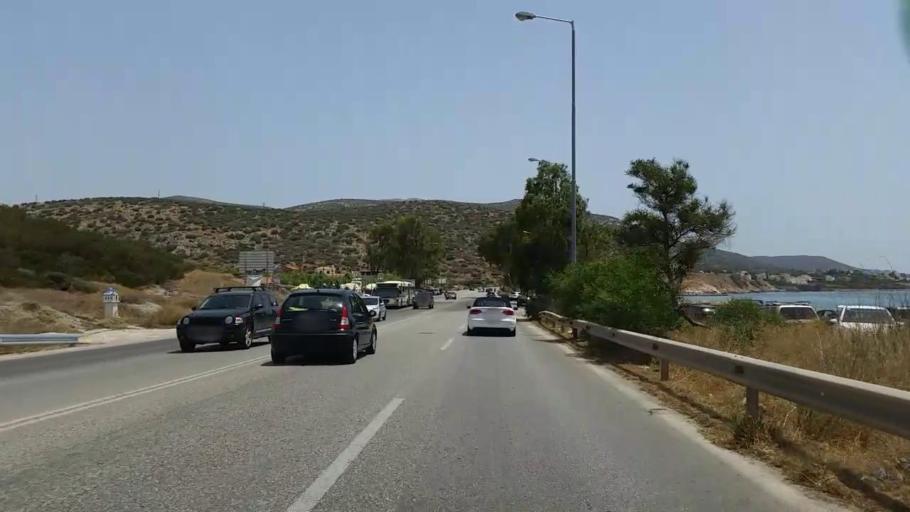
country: GR
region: Attica
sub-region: Nomarchia Anatolikis Attikis
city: Saronida
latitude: 37.7764
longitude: 23.8992
